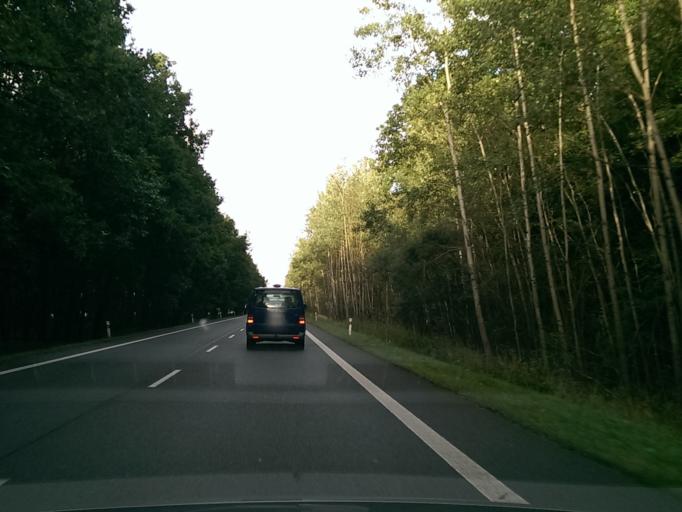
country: CZ
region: Central Bohemia
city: Knezmost
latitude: 50.4397
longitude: 15.0570
